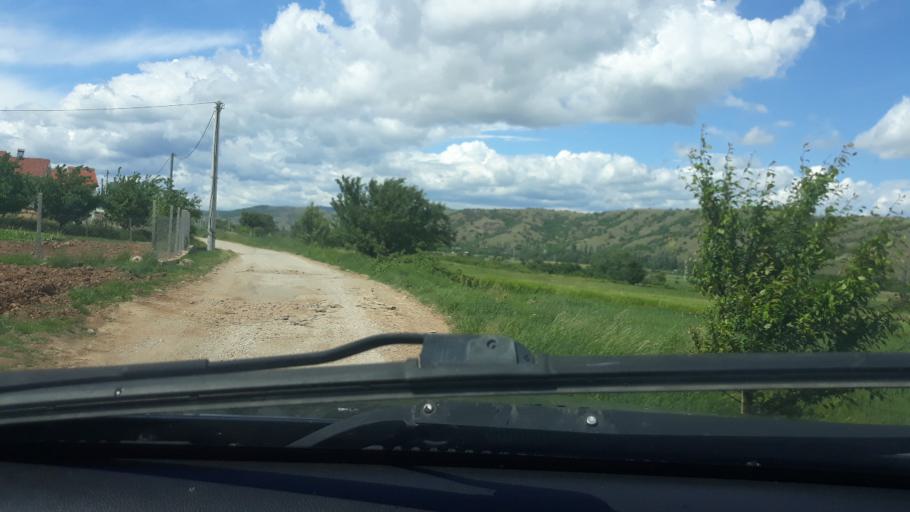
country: MK
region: Krivogastani
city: Krivogashtani
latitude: 41.3361
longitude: 21.3010
